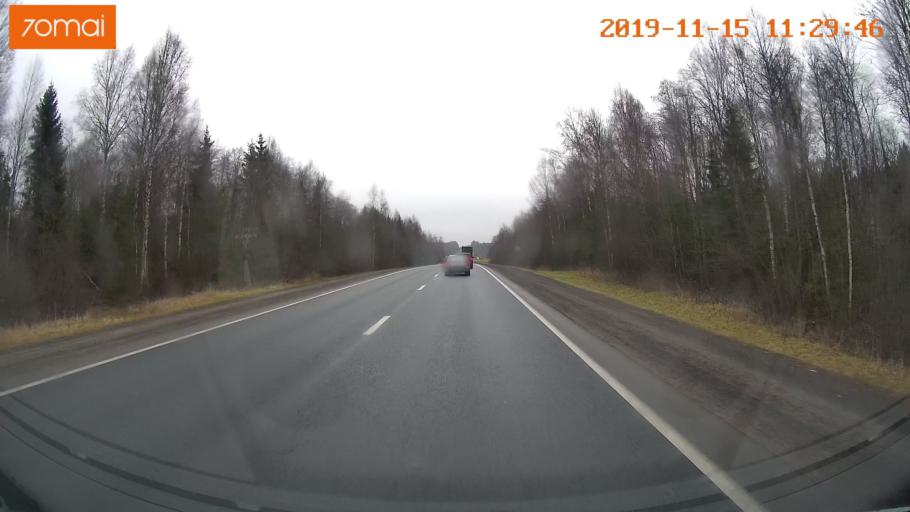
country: RU
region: Vologda
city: Molochnoye
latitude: 59.1765
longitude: 39.5179
